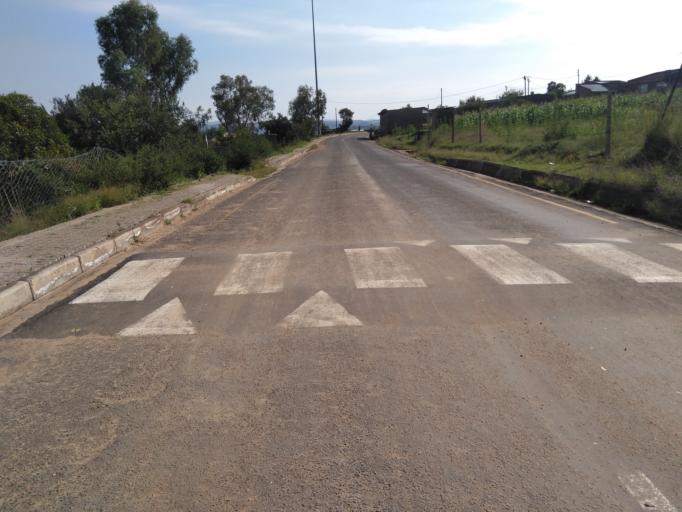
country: LS
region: Butha-Buthe
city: Butha-Buthe
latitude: -28.7764
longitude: 28.2457
